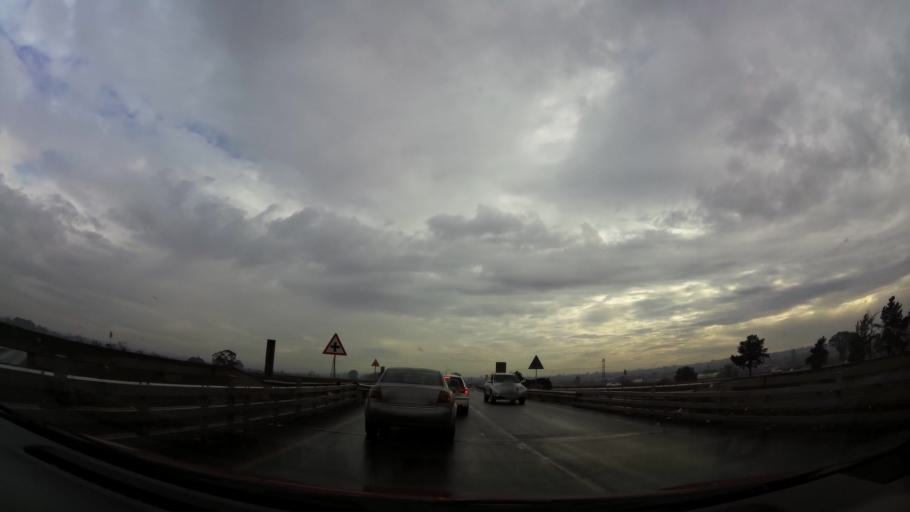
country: ZA
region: Gauteng
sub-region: City of Johannesburg Metropolitan Municipality
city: Soweto
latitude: -26.2968
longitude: 27.8471
